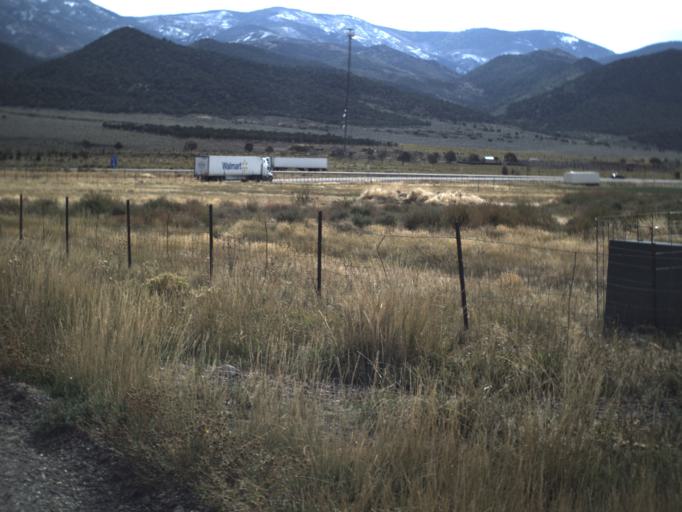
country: US
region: Utah
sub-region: Beaver County
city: Beaver
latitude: 38.5379
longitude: -112.6136
